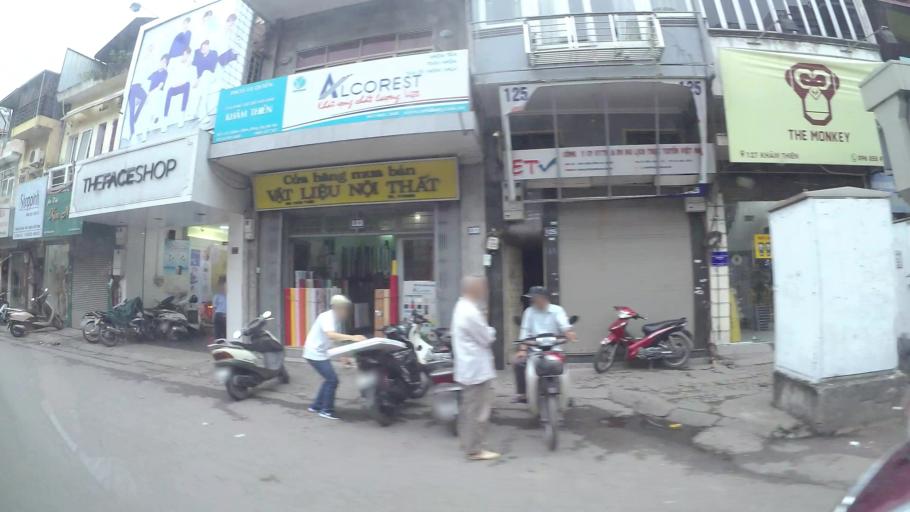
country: VN
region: Ha Noi
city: Dong Da
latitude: 21.0191
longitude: 105.8363
